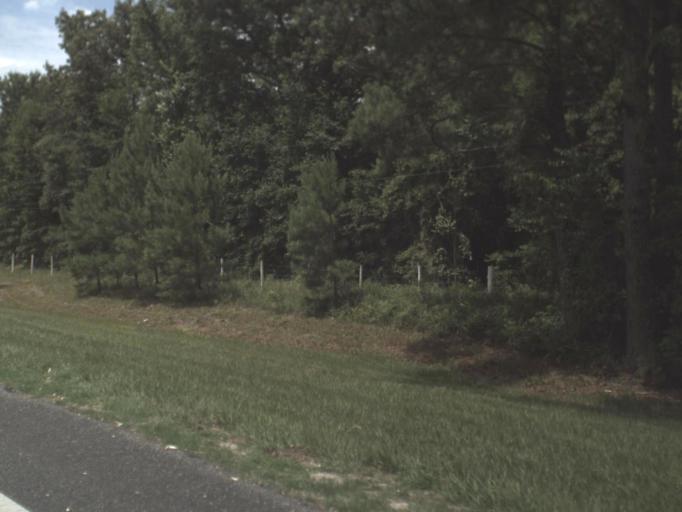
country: US
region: Florida
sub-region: Suwannee County
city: Live Oak
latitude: 30.1841
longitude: -82.9875
